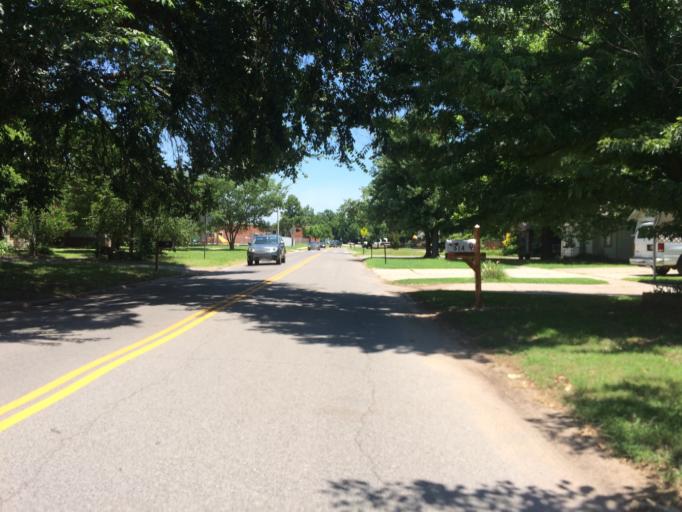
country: US
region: Oklahoma
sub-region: Cleveland County
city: Norman
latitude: 35.2250
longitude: -97.4364
